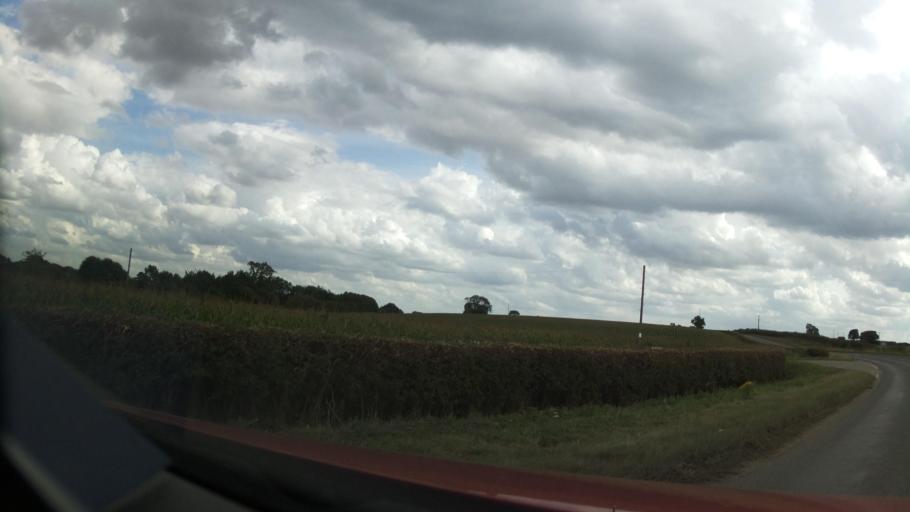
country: GB
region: England
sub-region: North Yorkshire
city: Ripon
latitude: 54.1746
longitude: -1.5533
